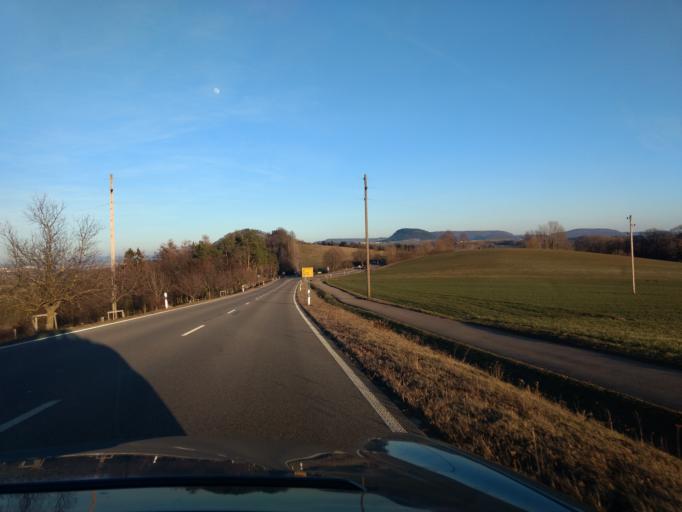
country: DE
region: Baden-Wuerttemberg
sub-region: Regierungsbezirk Stuttgart
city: Ottenbach
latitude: 48.7512
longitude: 9.7354
